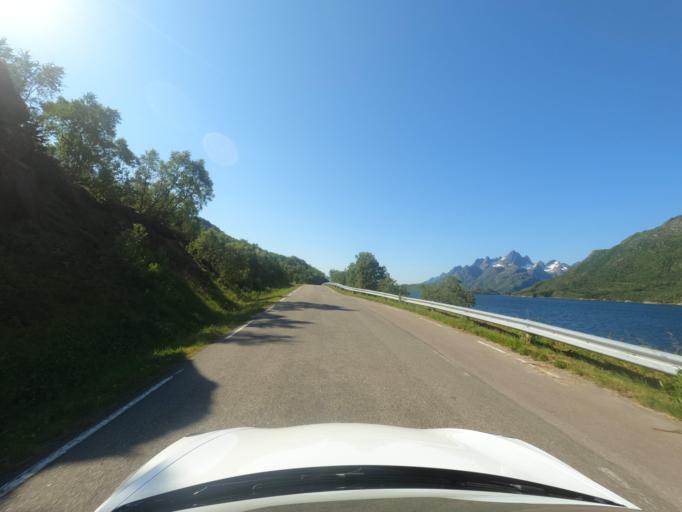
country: NO
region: Nordland
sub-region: Hadsel
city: Stokmarknes
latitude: 68.3787
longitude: 15.0841
